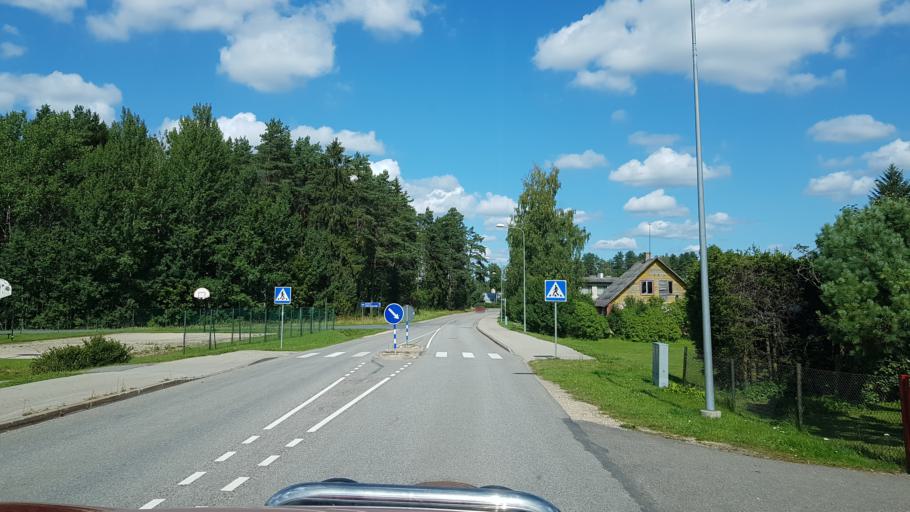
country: EE
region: Vorumaa
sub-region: Voru linn
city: Voru
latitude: 57.7293
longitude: 27.2733
